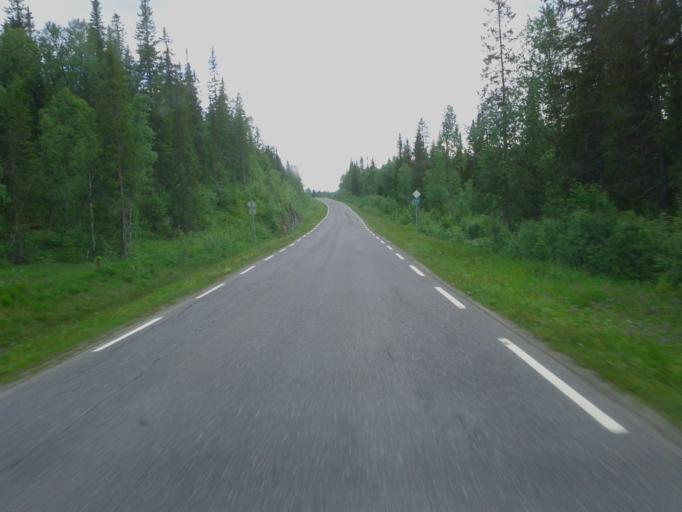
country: NO
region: Nordland
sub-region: Hattfjelldal
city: Hattfjelldal
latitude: 65.5563
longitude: 13.7465
